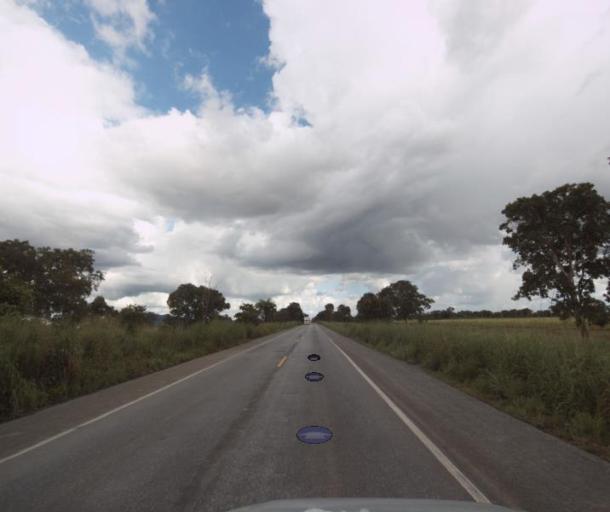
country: BR
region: Goias
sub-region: Porangatu
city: Porangatu
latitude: -13.2870
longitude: -49.1260
